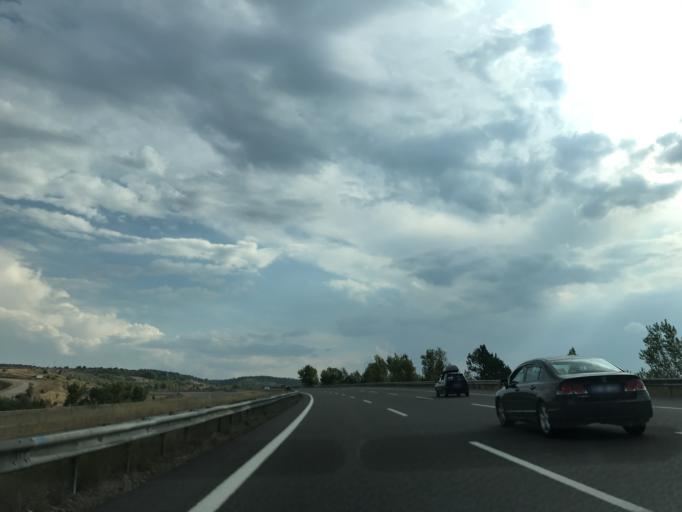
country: TR
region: Bolu
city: Gerede
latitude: 40.6610
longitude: 32.2380
